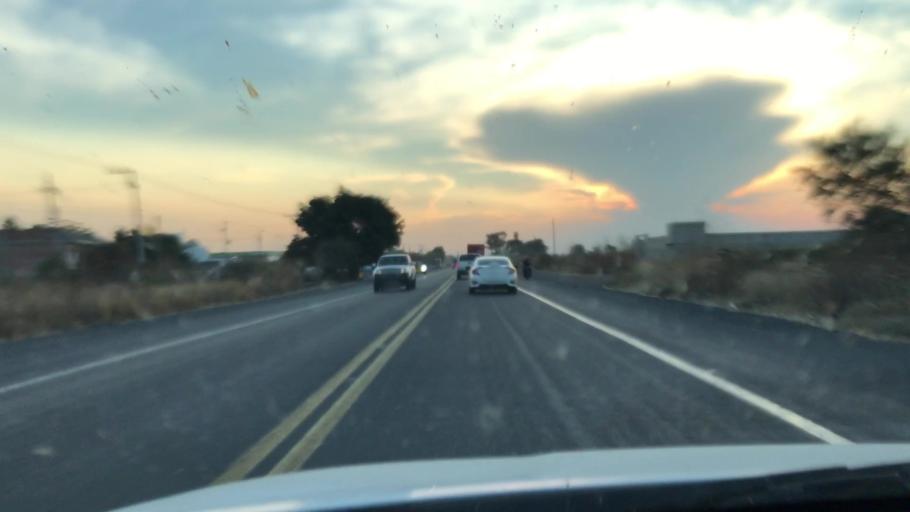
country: MX
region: Michoacan
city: Tanhuato de Guerrero
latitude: 20.3035
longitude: -102.3199
